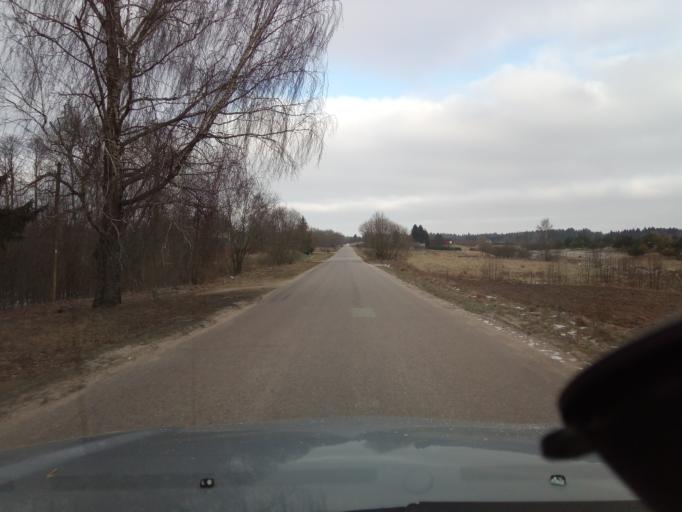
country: LT
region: Alytaus apskritis
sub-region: Alytaus rajonas
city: Daugai
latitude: 54.3486
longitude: 24.2573
